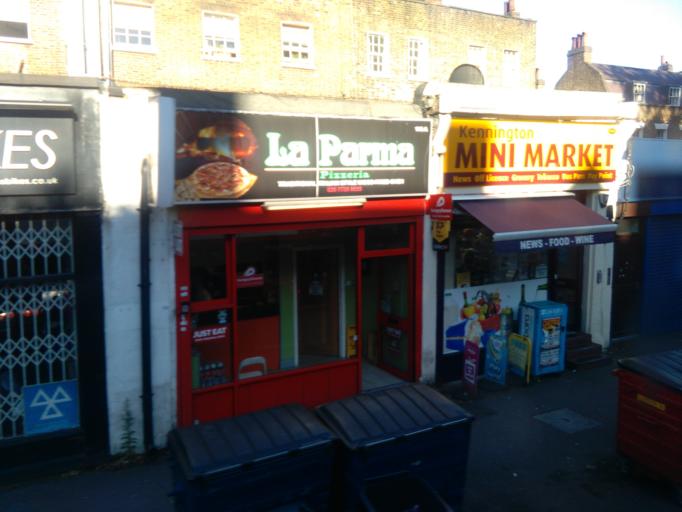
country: GB
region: England
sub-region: Greater London
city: Lambeth
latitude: 51.4953
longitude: -0.1108
